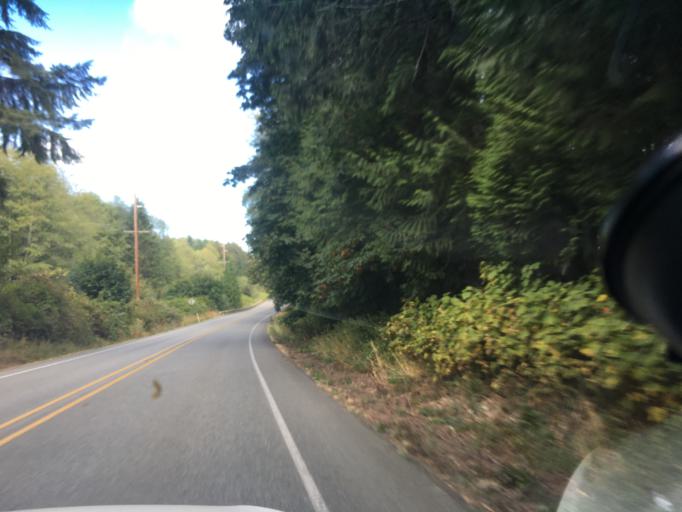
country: US
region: Washington
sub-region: Kitsap County
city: Lofall
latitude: 47.8406
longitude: -122.5873
